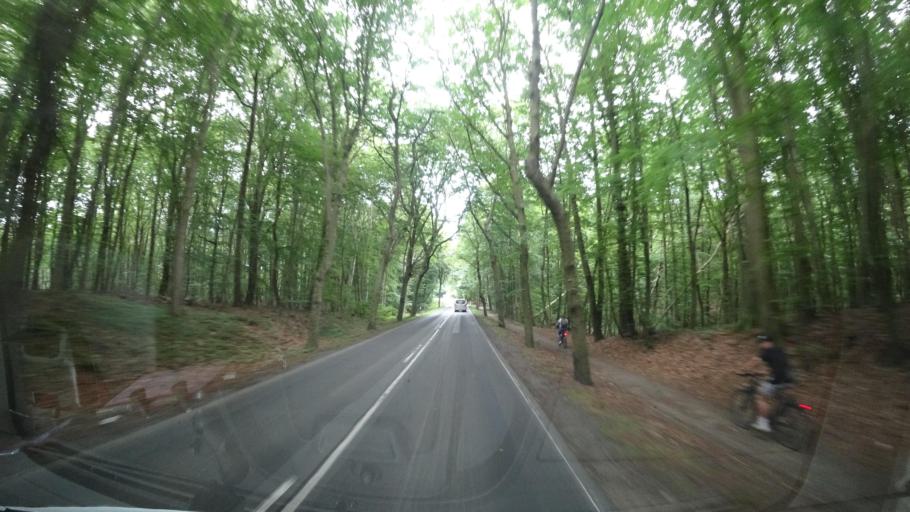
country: DE
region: Mecklenburg-Vorpommern
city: Putbus
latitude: 54.3483
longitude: 13.4486
